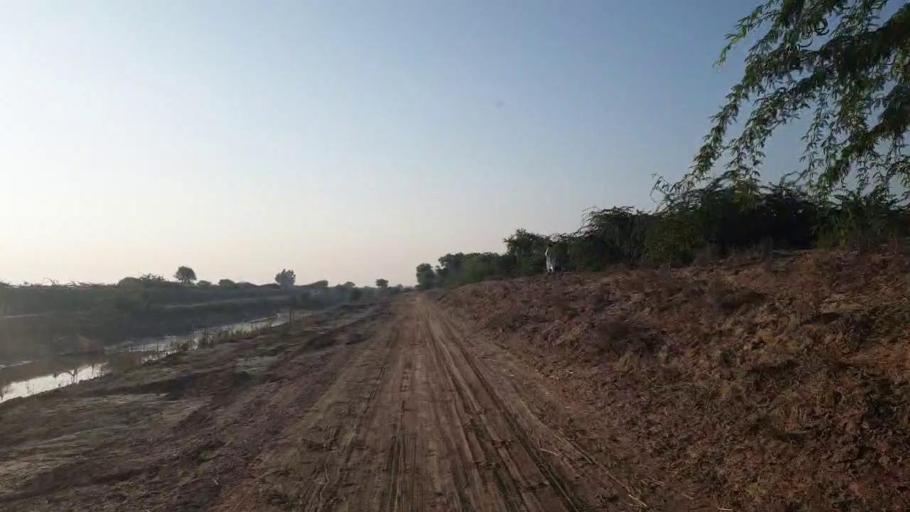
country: PK
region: Sindh
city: Badin
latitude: 24.6470
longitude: 68.7900
